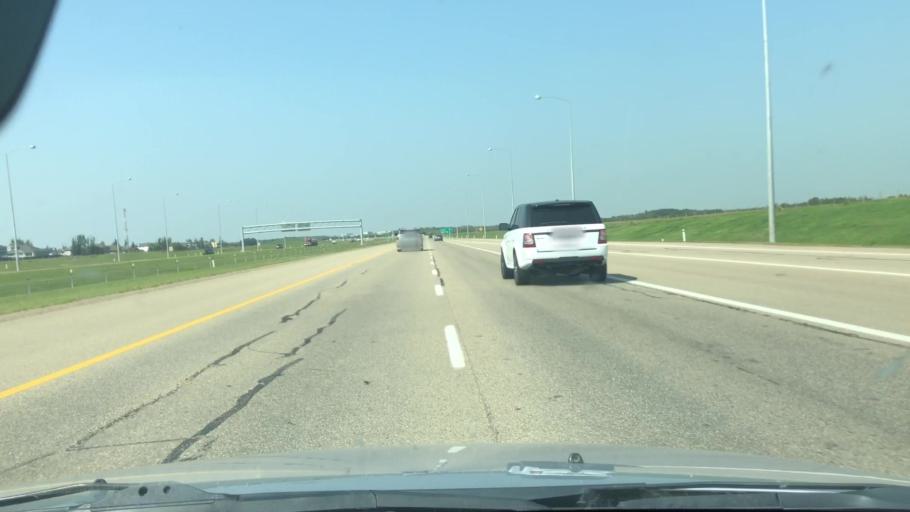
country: CA
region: Alberta
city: Edmonton
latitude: 53.6472
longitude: -113.4976
